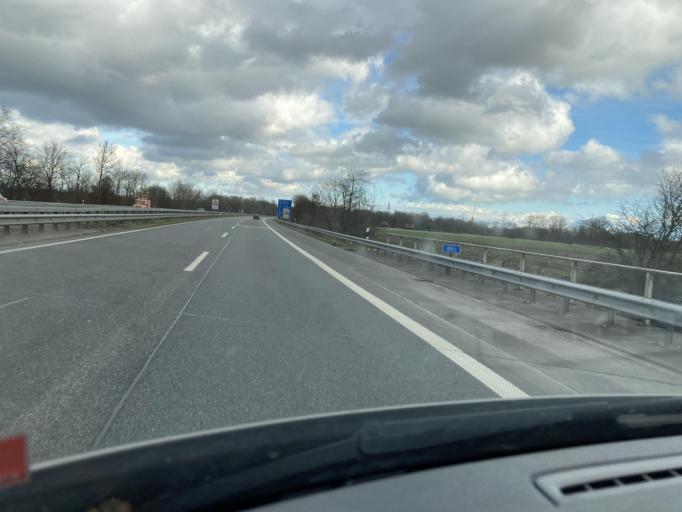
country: DE
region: Lower Saxony
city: Fedderwarden
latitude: 53.5555
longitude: 8.0682
